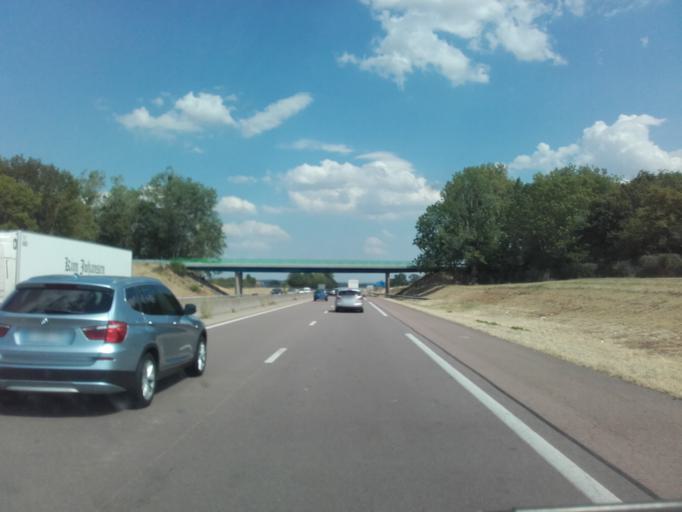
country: FR
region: Bourgogne
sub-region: Departement de l'Yonne
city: Avallon
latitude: 47.5050
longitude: 4.0700
